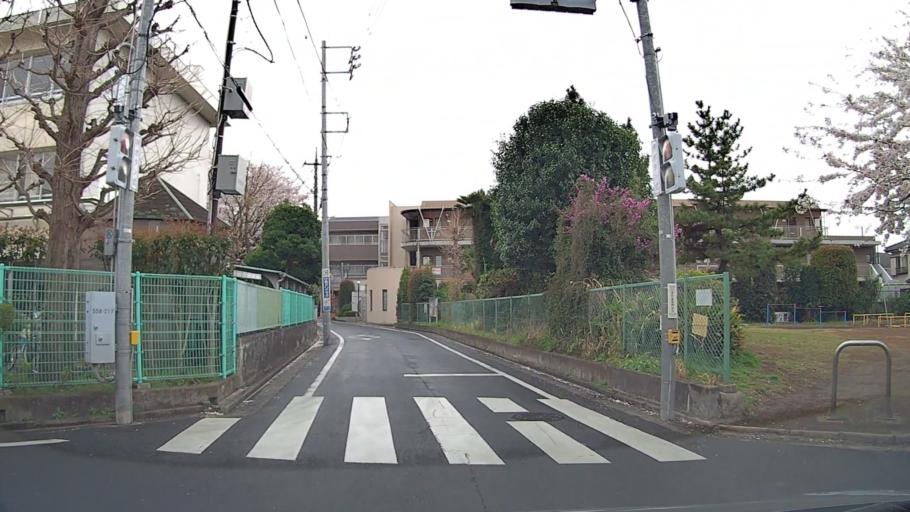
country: JP
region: Tokyo
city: Musashino
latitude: 35.7453
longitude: 139.5805
